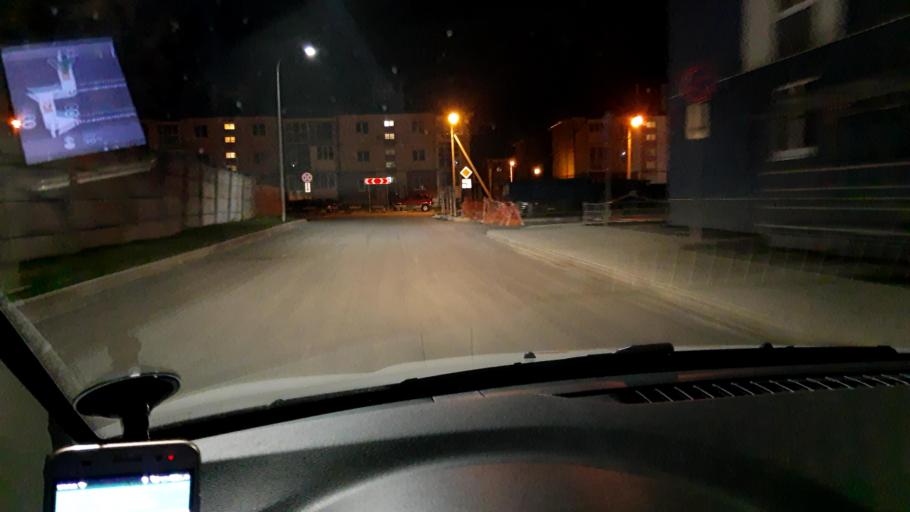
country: RU
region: Nizjnij Novgorod
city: Burevestnik
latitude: 56.2074
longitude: 43.8194
